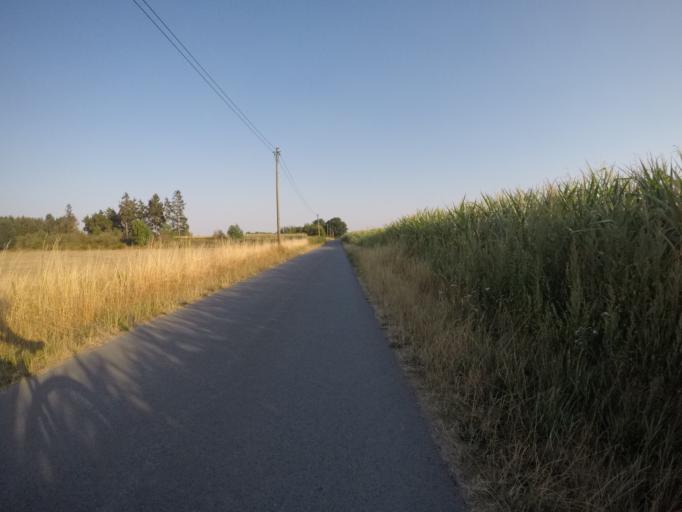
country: NL
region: Gelderland
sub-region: Gemeente Aalten
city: Aalten
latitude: 51.8718
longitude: 6.5423
